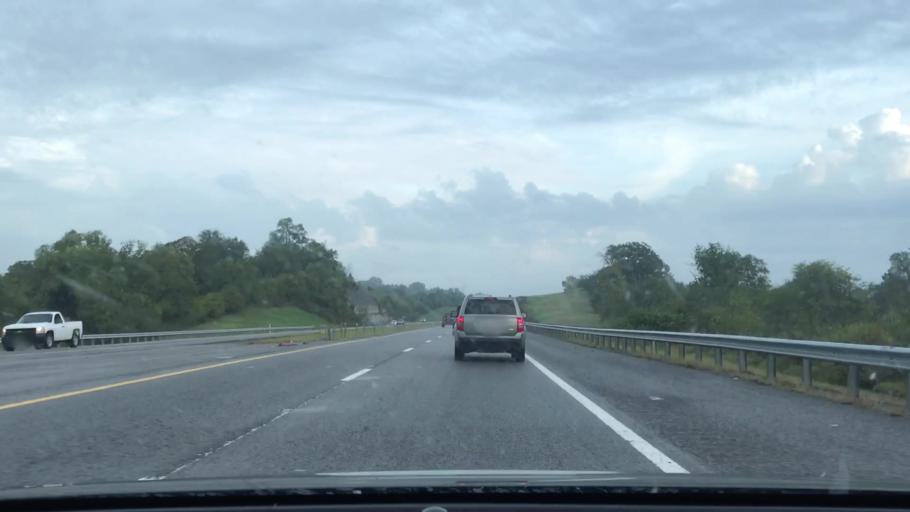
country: US
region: Tennessee
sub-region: Sumner County
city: Shackle Island
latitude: 36.3373
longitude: -86.5491
